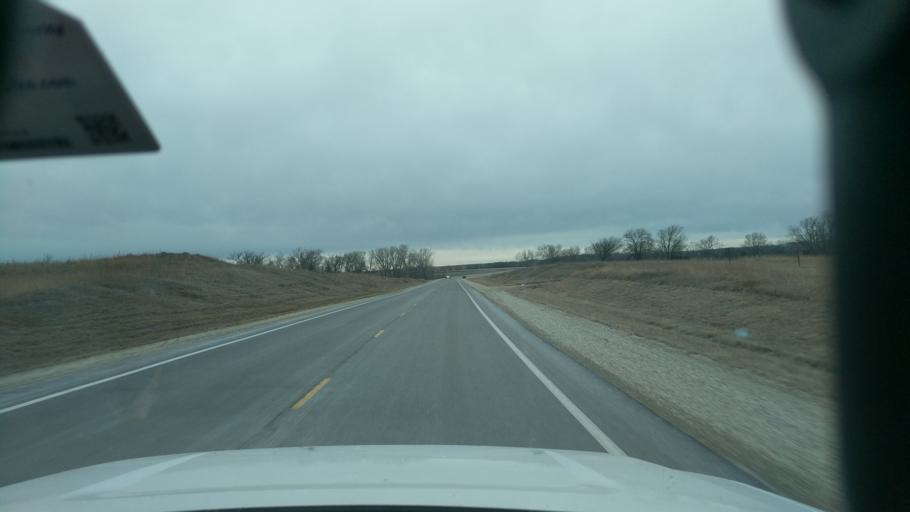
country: US
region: Kansas
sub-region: Marion County
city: Marion
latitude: 38.4288
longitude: -96.9588
